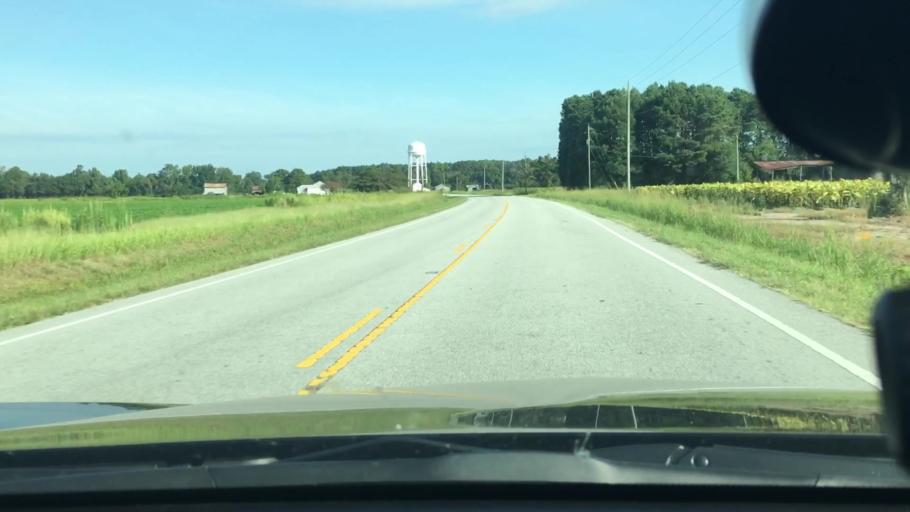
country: US
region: North Carolina
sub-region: Pitt County
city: Farmville
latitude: 35.7066
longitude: -77.5181
